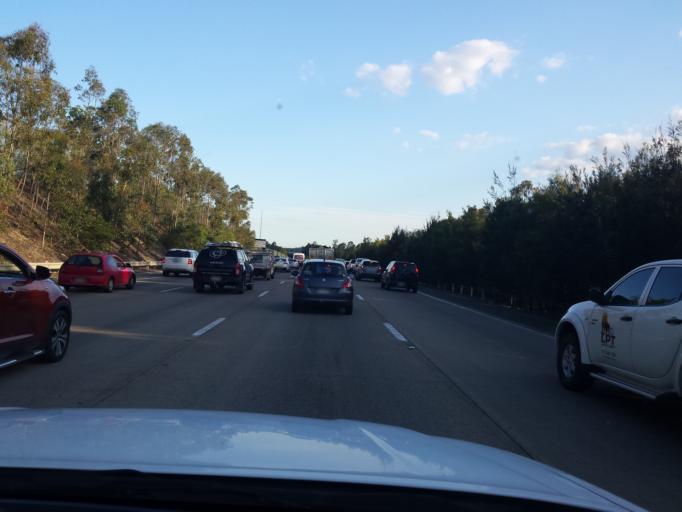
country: AU
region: Queensland
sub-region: Gold Coast
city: Oxenford
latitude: -27.8406
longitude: 153.3038
